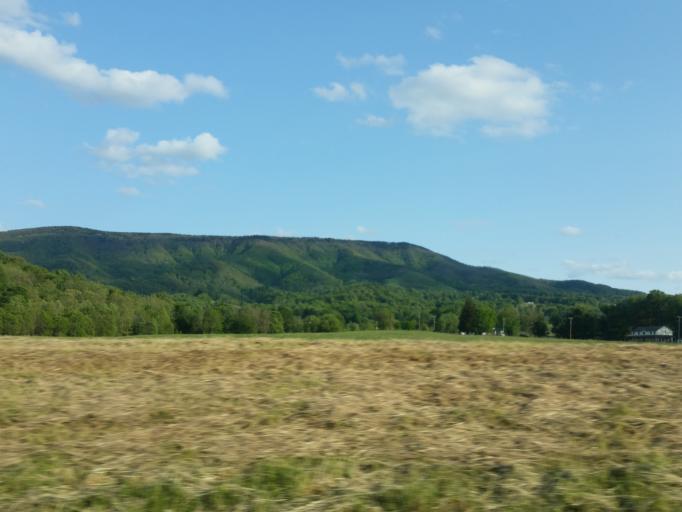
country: US
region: Virginia
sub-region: Russell County
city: Honaker
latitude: 36.9693
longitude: -81.9075
